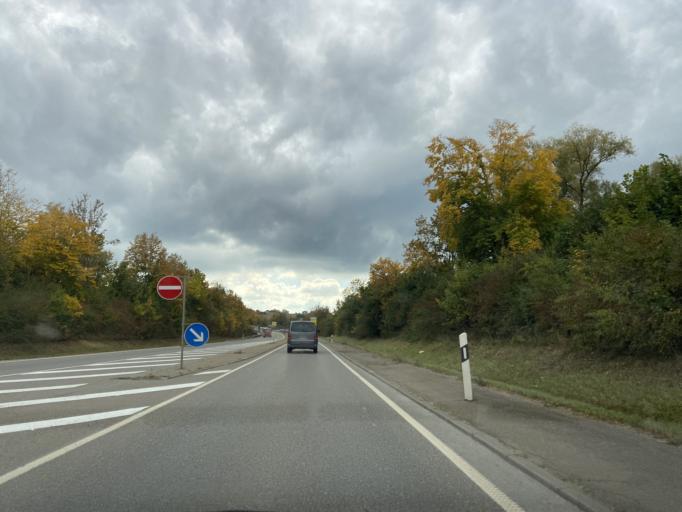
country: DE
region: Baden-Wuerttemberg
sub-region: Tuebingen Region
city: Sigmaringen
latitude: 48.0808
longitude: 9.2064
